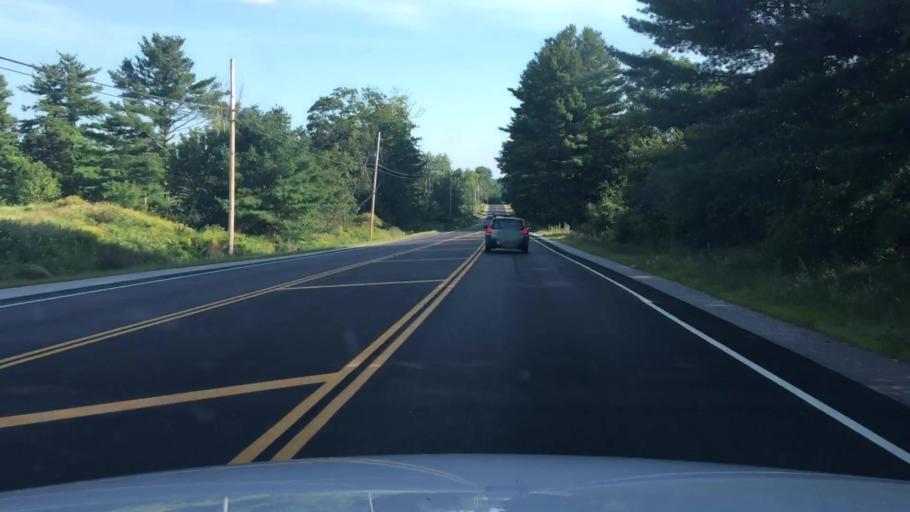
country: US
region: Maine
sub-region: Cumberland County
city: Cumberland Center
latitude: 43.8061
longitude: -70.3105
